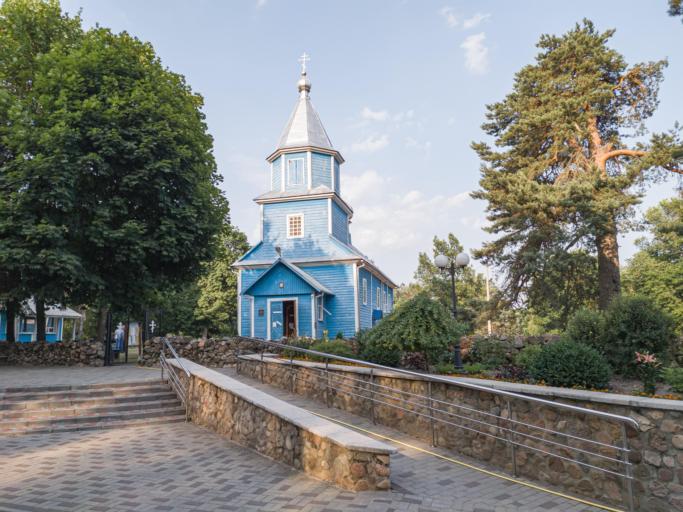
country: BY
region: Brest
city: Zhabinka
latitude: 52.4058
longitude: 24.0890
